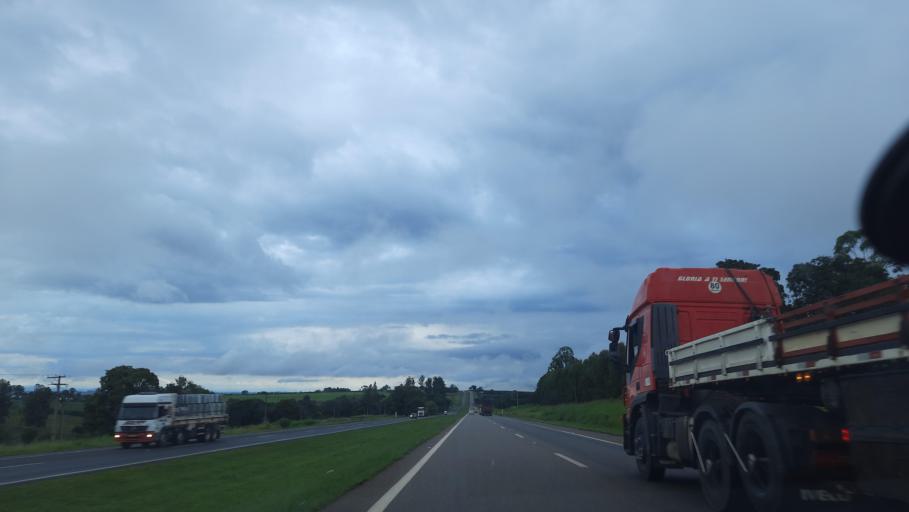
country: BR
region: Sao Paulo
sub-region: Moji-Guacu
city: Mogi-Gaucu
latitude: -22.2344
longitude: -46.9786
